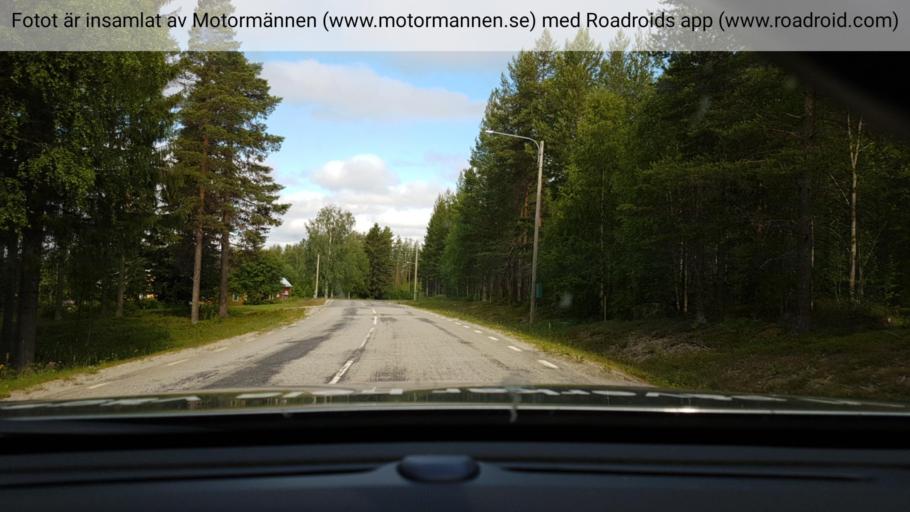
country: SE
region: Vaesterbotten
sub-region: Norsjo Kommun
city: Norsjoe
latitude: 64.7162
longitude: 19.1403
